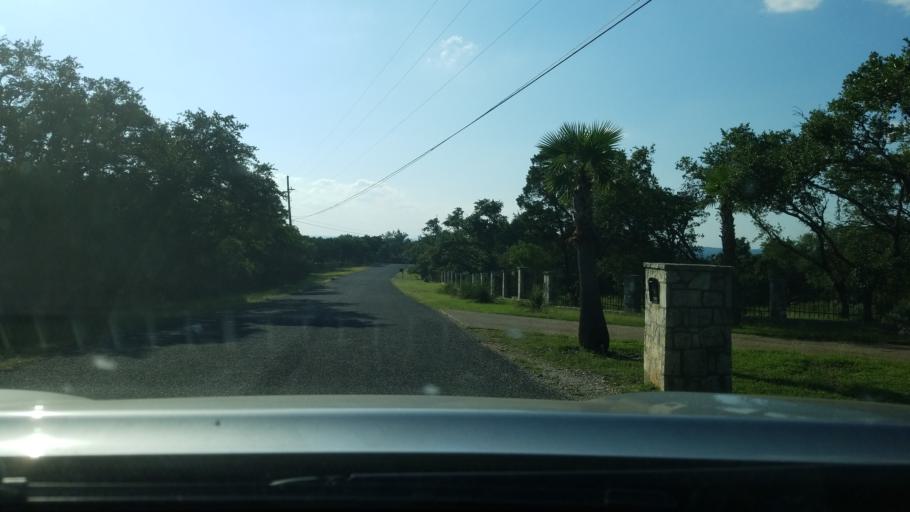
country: US
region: Texas
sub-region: Bexar County
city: Timberwood Park
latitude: 29.7076
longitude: -98.4442
